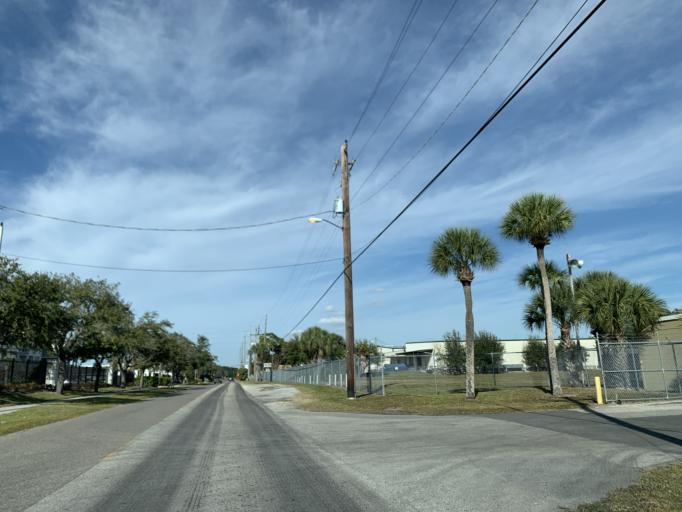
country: US
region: Florida
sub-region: Hillsborough County
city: Tampa
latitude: 27.8886
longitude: -82.5154
